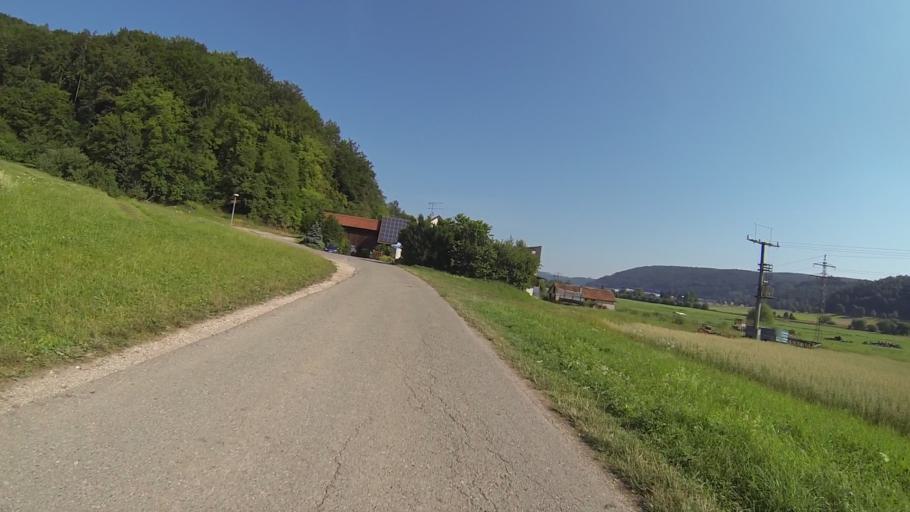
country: DE
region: Baden-Wuerttemberg
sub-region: Regierungsbezirk Stuttgart
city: Konigsbronn
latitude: 48.7519
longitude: 10.0966
